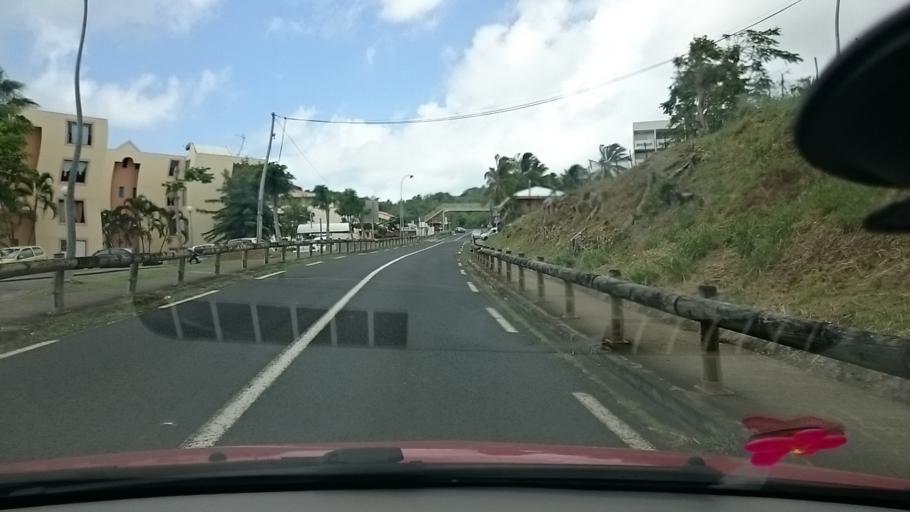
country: MQ
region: Martinique
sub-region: Martinique
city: La Trinite
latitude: 14.7452
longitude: -60.9466
